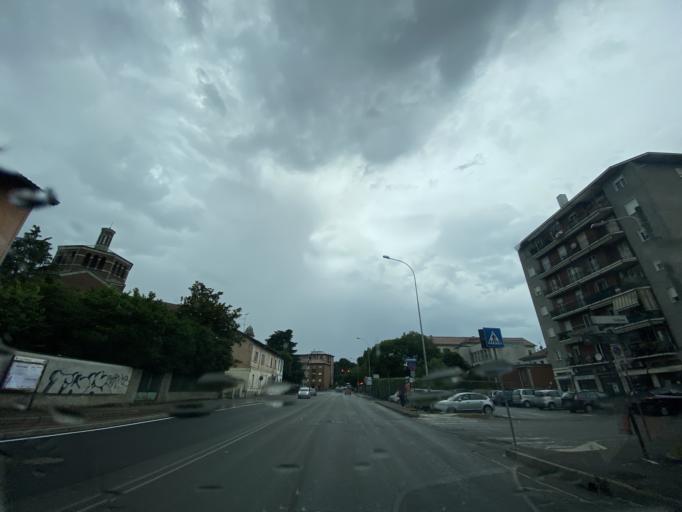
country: IT
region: Lombardy
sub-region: Provincia di Monza e Brianza
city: Monza
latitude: 45.5628
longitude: 9.2661
